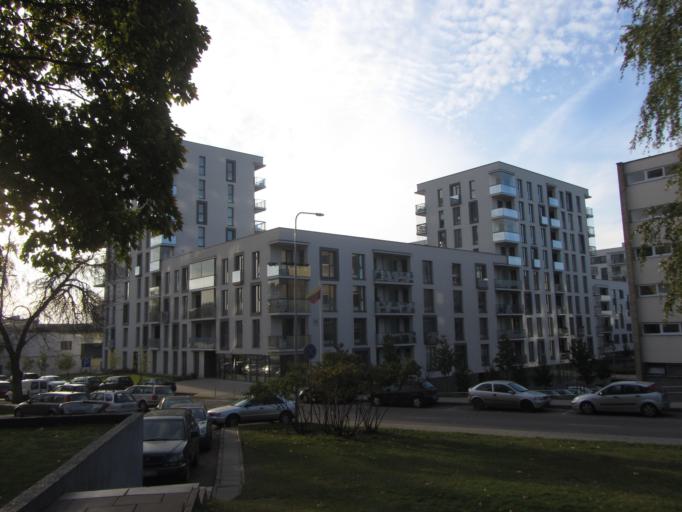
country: LT
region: Vilnius County
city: Naujamiestis
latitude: 54.6780
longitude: 25.2605
